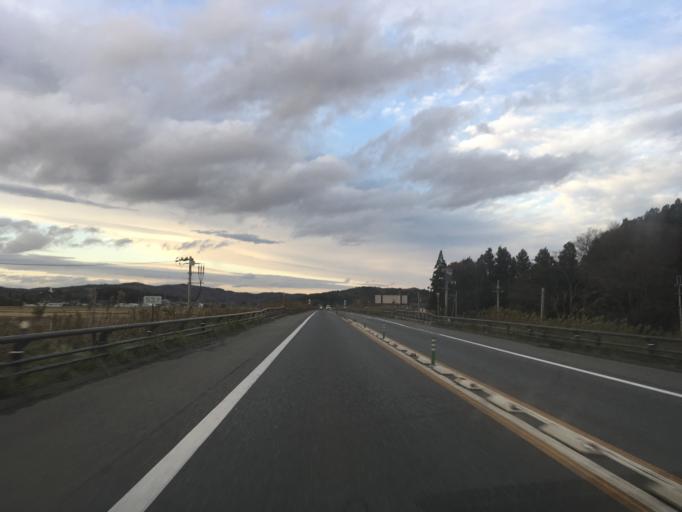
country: JP
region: Miyagi
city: Wakuya
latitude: 38.5785
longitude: 141.2739
